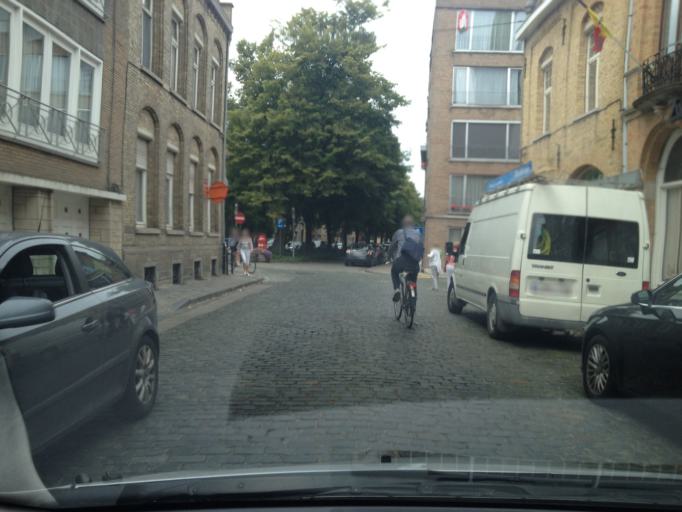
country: BE
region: Flanders
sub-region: Provincie West-Vlaanderen
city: Ieper
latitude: 50.8528
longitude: 2.8834
